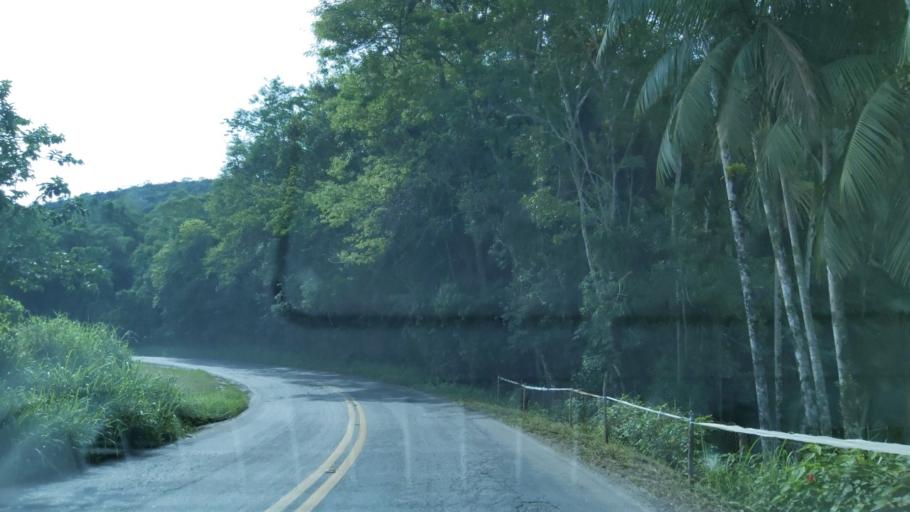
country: BR
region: Sao Paulo
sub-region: Miracatu
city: Miracatu
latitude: -24.0583
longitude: -47.5774
